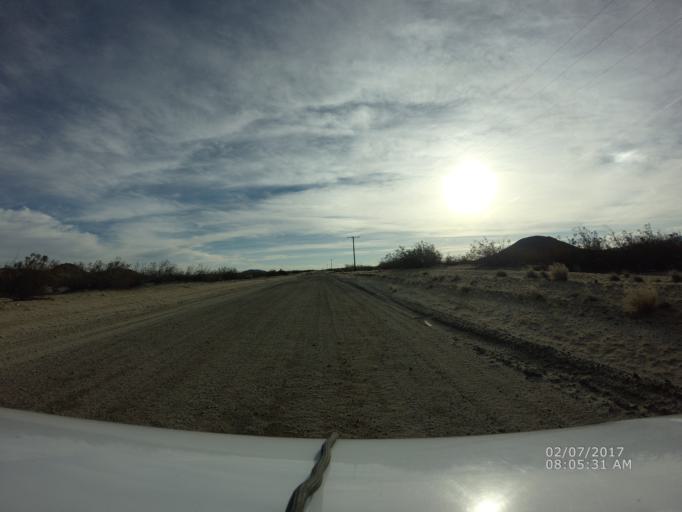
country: US
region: California
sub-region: Los Angeles County
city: Lake Los Angeles
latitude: 34.5725
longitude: -117.7447
